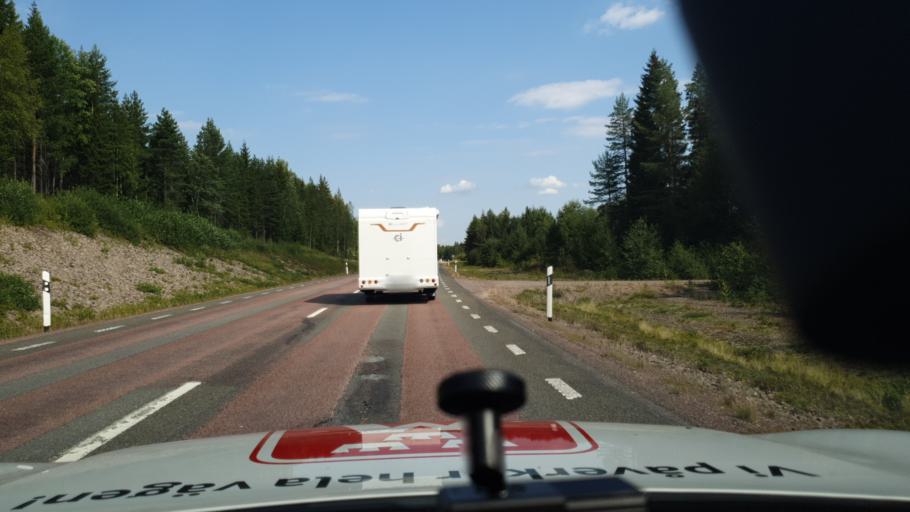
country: SE
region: Dalarna
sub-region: Malung-Saelens kommun
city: Malung
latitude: 60.6220
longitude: 13.6093
